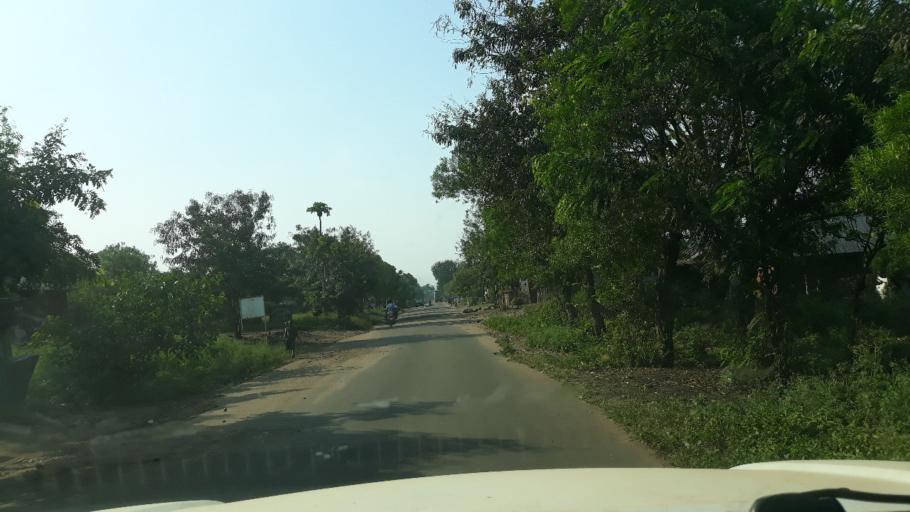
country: BI
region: Cibitoke
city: Cibitoke
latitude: -2.7919
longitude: 28.9998
